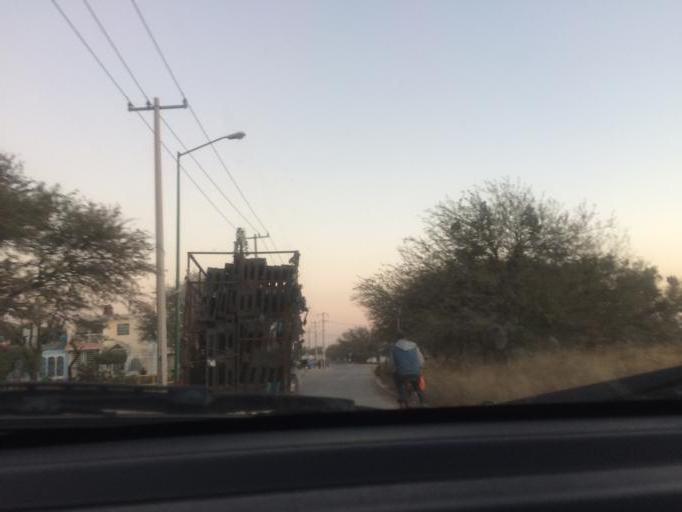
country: MX
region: Guanajuato
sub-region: Leon
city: Fraccionamiento Paraiso Real
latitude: 21.1211
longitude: -101.5914
